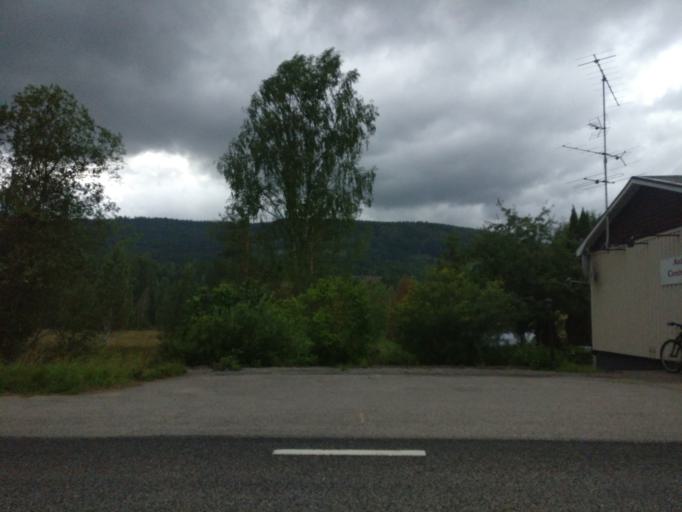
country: SE
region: Vaermland
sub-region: Torsby Kommun
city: Torsby
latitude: 60.7293
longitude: 12.8719
